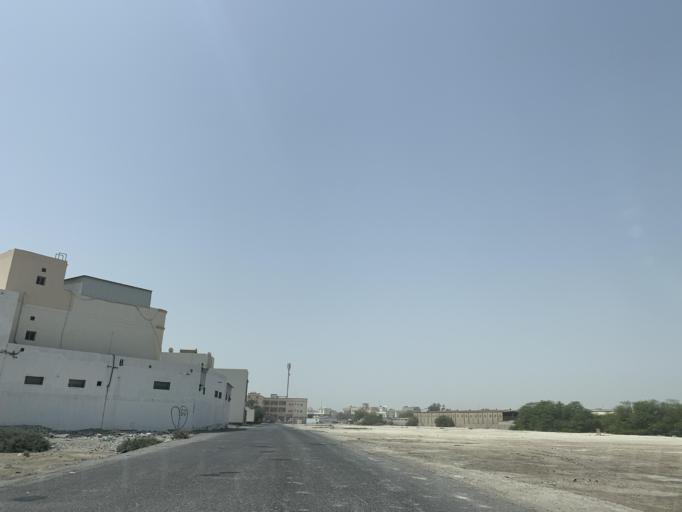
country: BH
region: Northern
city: Madinat `Isa
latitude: 26.1674
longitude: 50.5199
